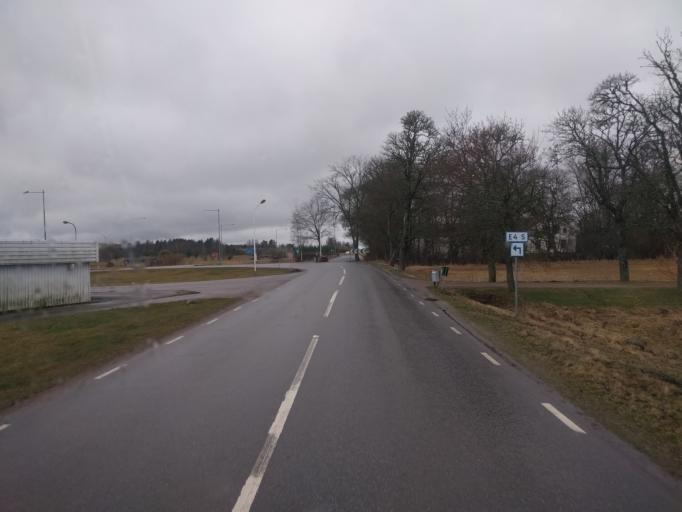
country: SE
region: OEstergoetland
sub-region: Vadstena Kommun
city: Herrestad
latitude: 58.3115
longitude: 14.9047
